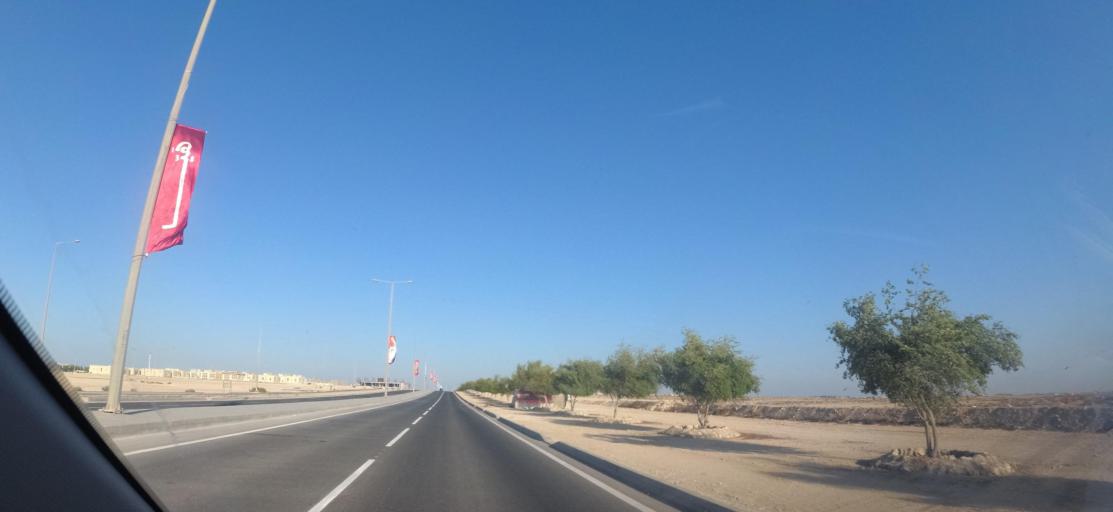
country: QA
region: Madinat ash Shamal
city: Ar Ru'ays
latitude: 26.1314
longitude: 51.2203
